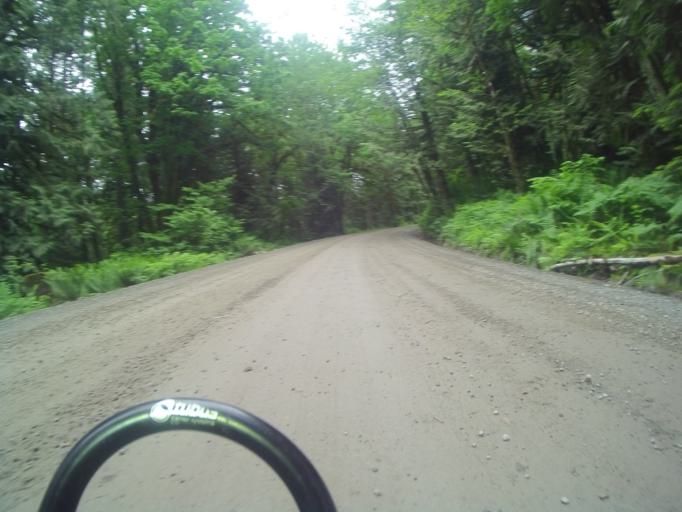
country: CA
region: British Columbia
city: Agassiz
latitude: 49.3305
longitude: -121.8723
